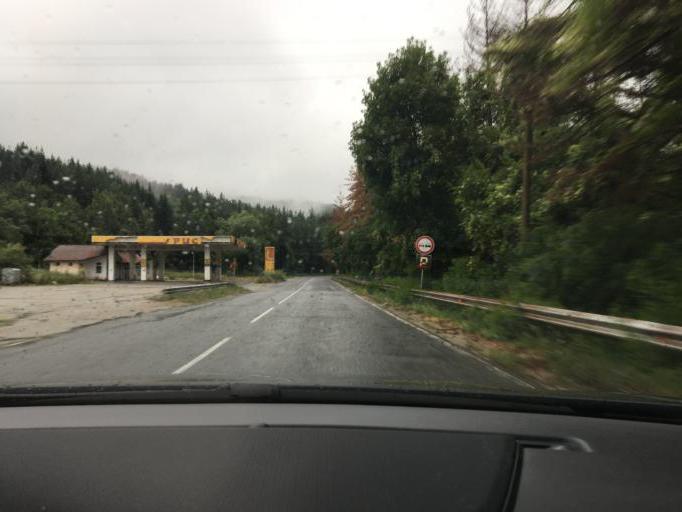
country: MK
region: Kriva Palanka
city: Kriva Palanka
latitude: 42.2254
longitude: 22.4811
